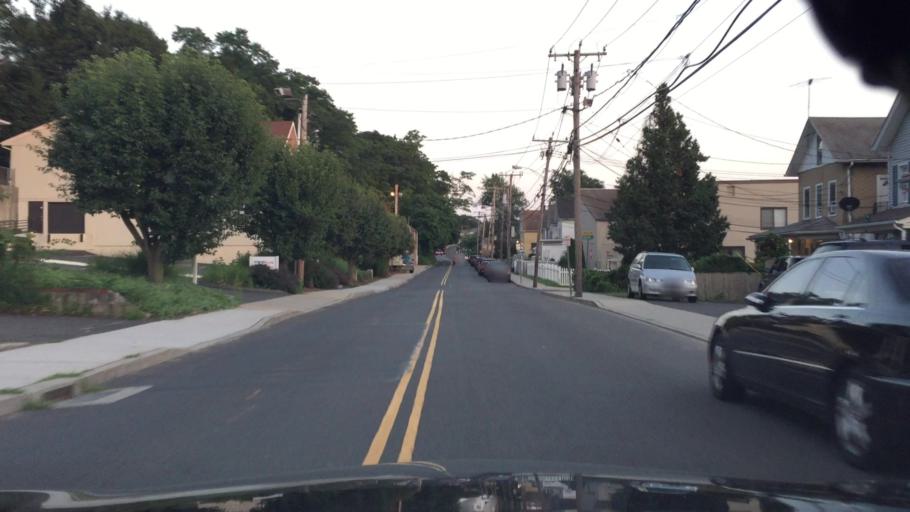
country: US
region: Connecticut
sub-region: Fairfield County
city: Norwalk
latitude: 41.1028
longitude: -73.4297
